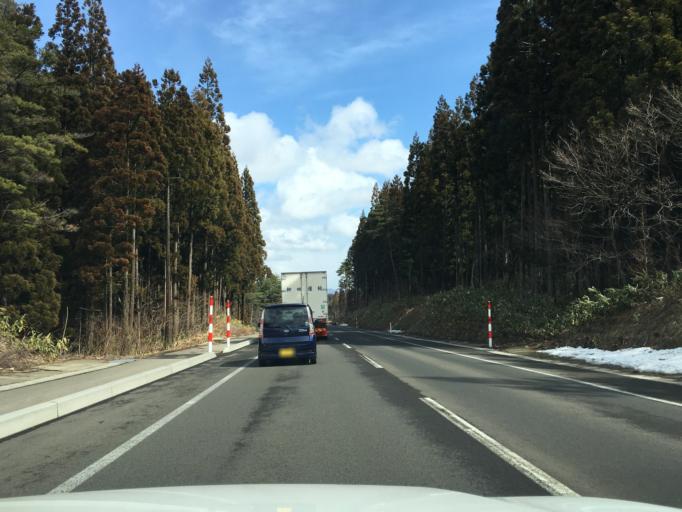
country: JP
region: Akita
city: Takanosu
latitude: 40.1081
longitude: 140.3551
